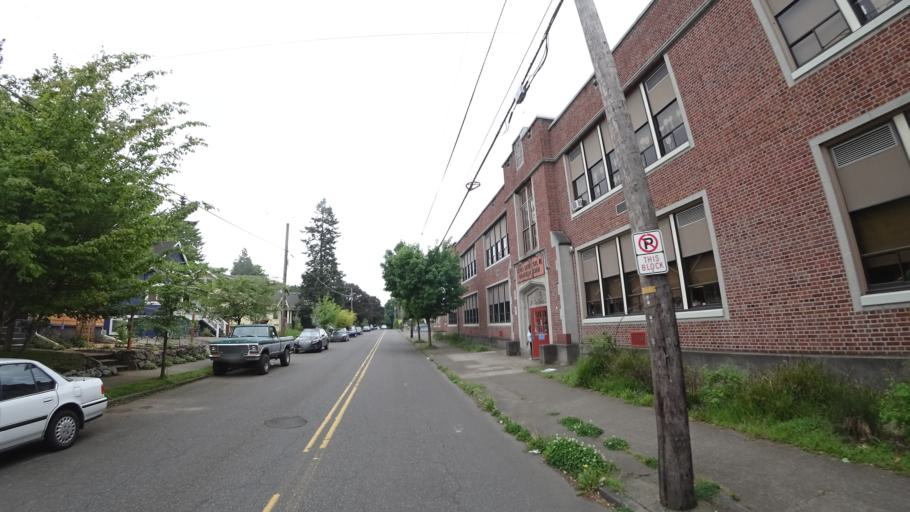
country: US
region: Oregon
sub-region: Multnomah County
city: Portland
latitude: 45.5585
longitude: -122.6586
